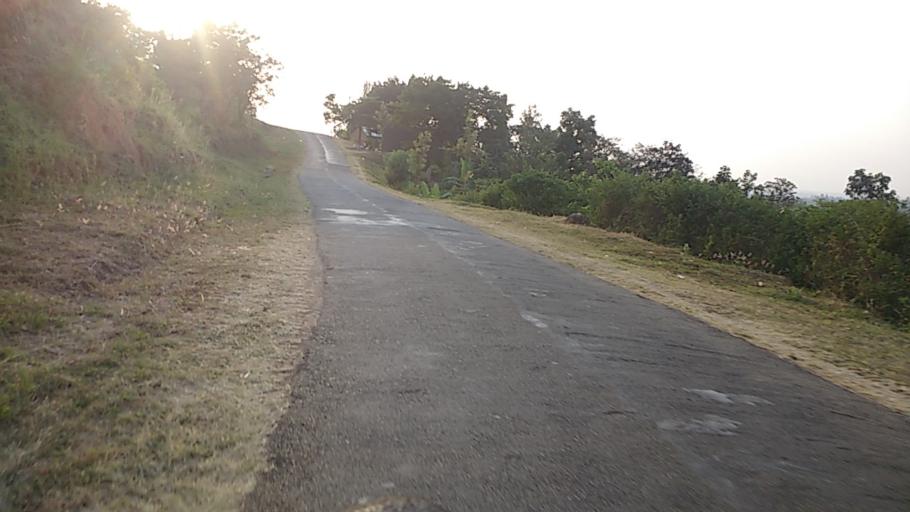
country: UG
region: Eastern Region
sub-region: Mbale District
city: Mbale
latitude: 1.0775
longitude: 34.2114
